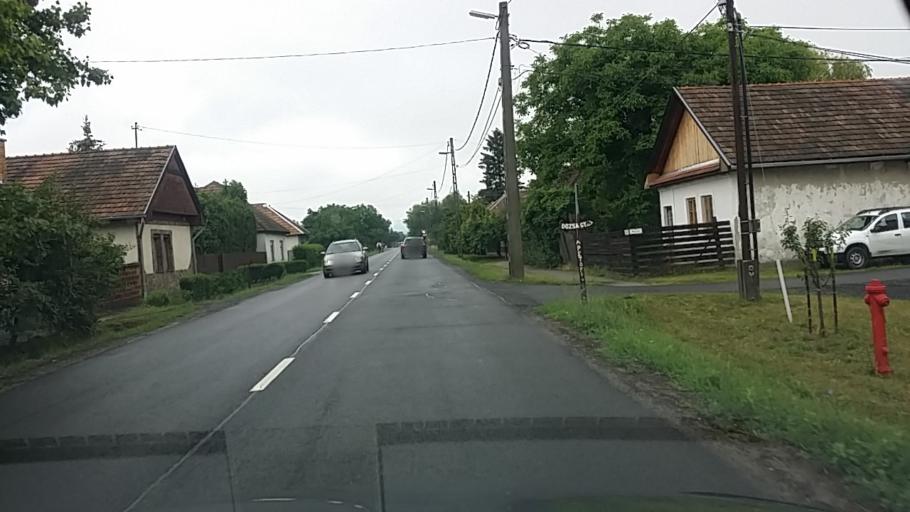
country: HU
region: Komarom-Esztergom
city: Esztergom
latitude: 47.9252
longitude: 18.7761
